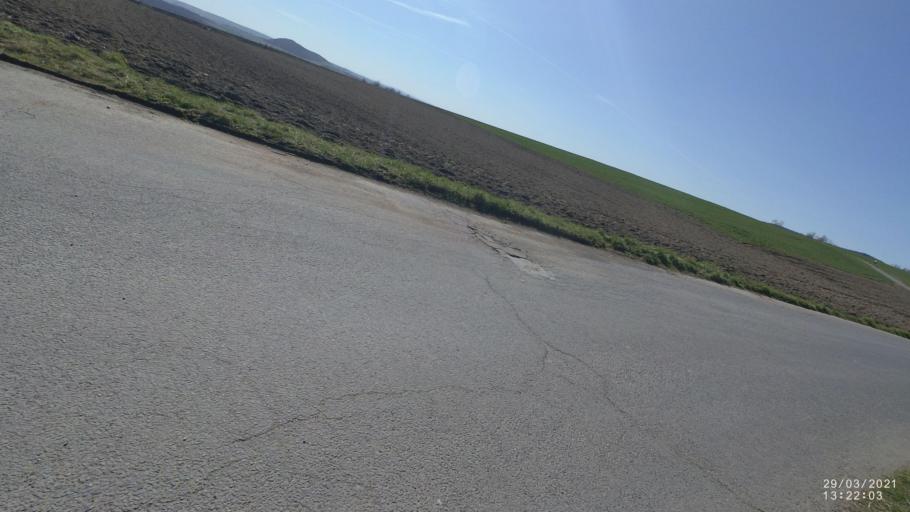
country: DE
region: Rheinland-Pfalz
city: Nickenich
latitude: 50.4215
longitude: 7.3458
